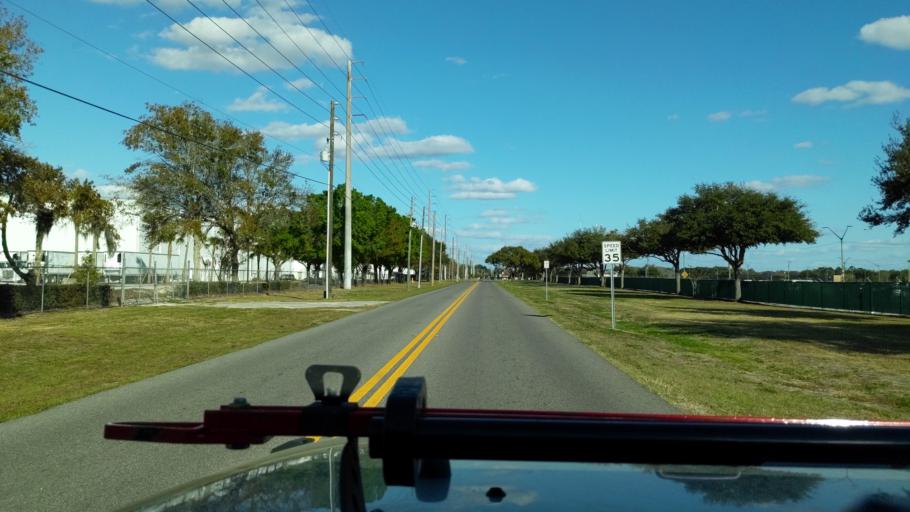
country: US
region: Florida
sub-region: Orange County
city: Ocoee
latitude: 28.5590
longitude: -81.5512
